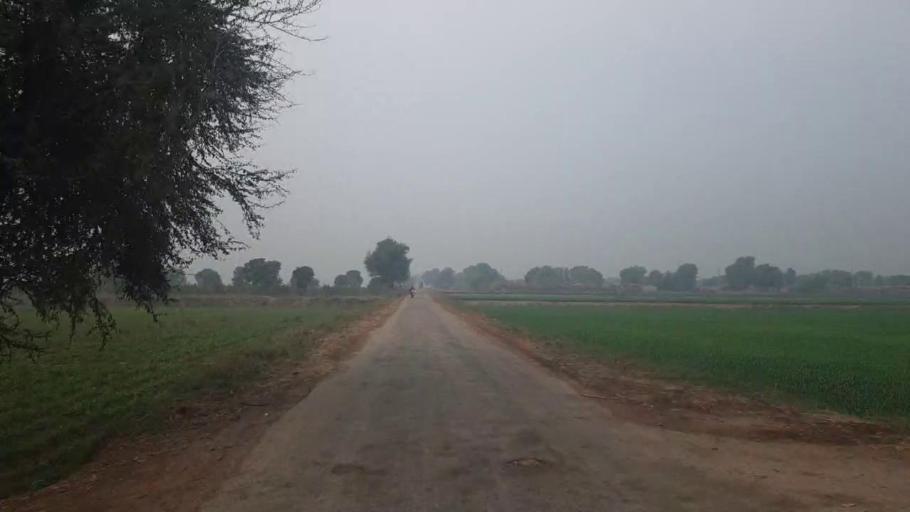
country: PK
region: Sindh
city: Tando Adam
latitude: 25.7098
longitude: 68.6645
